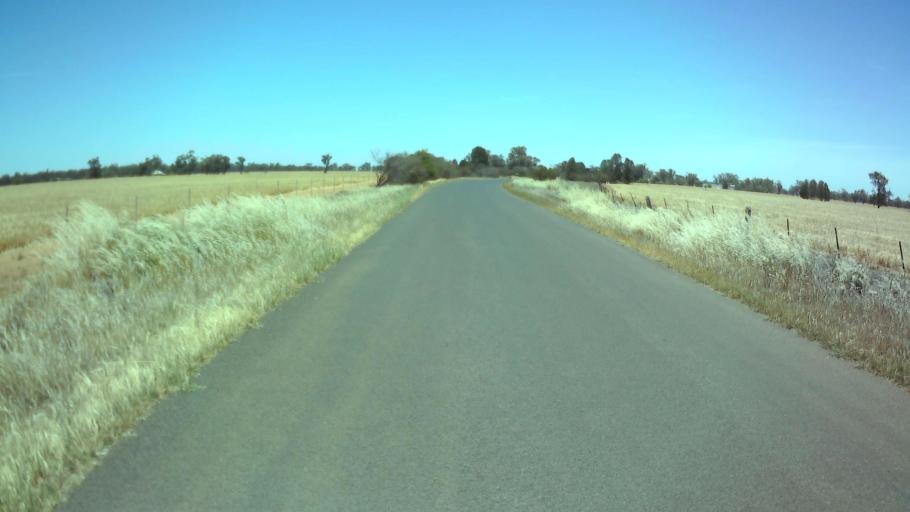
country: AU
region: New South Wales
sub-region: Weddin
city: Grenfell
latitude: -34.0550
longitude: 147.7809
